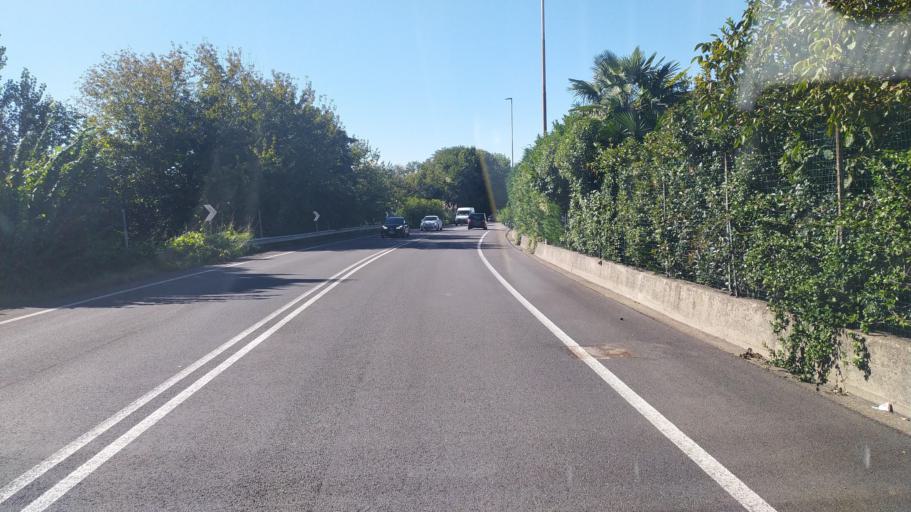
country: IT
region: Lombardy
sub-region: Provincia di Varese
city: Varese
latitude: 45.8128
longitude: 8.8147
